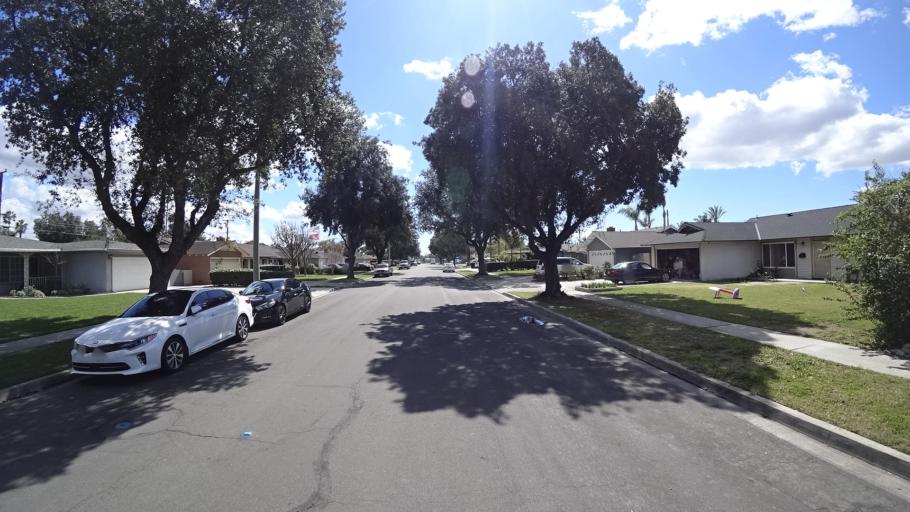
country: US
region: California
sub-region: Orange County
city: Anaheim
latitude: 33.8286
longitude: -117.8935
